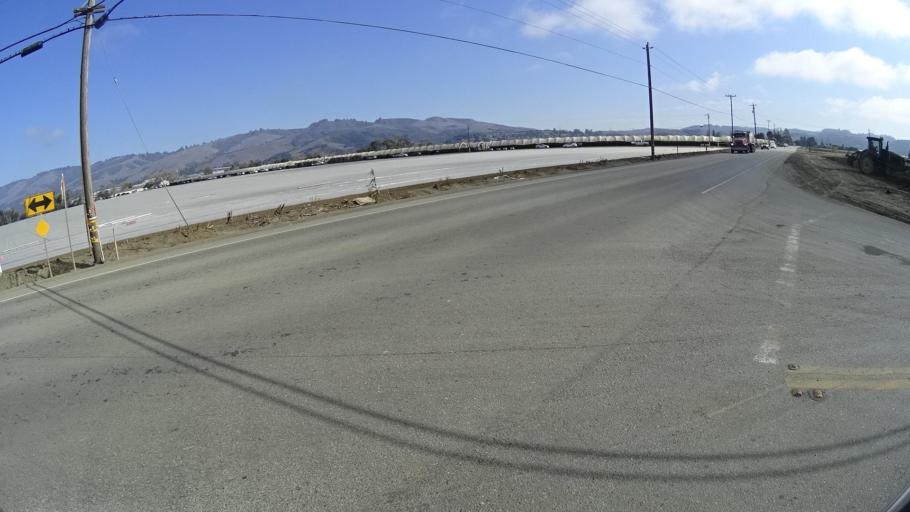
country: US
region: California
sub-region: San Benito County
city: Aromas
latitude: 36.9000
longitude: -121.6908
